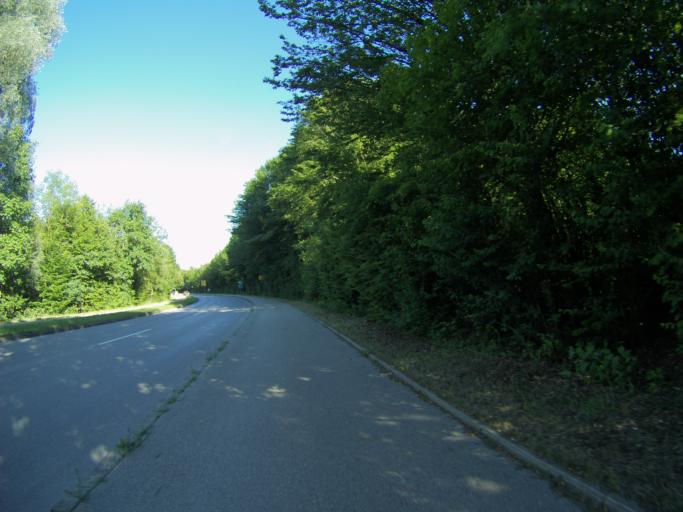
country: DE
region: Bavaria
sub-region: Upper Bavaria
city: Freising
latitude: 48.4097
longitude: 11.7252
